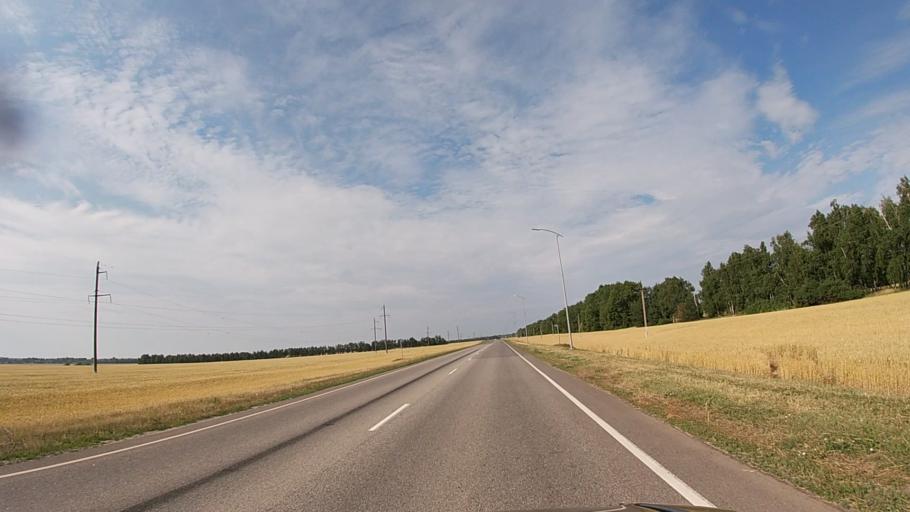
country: RU
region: Belgorod
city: Proletarskiy
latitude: 50.8185
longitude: 35.7547
